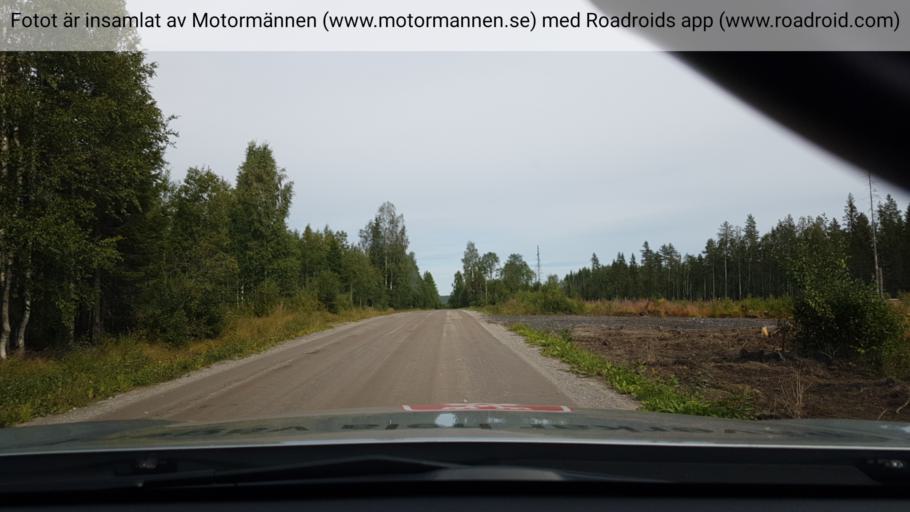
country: SE
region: Vaesterbotten
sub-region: Vannas Kommun
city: Vaennaes
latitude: 63.7974
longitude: 19.6298
